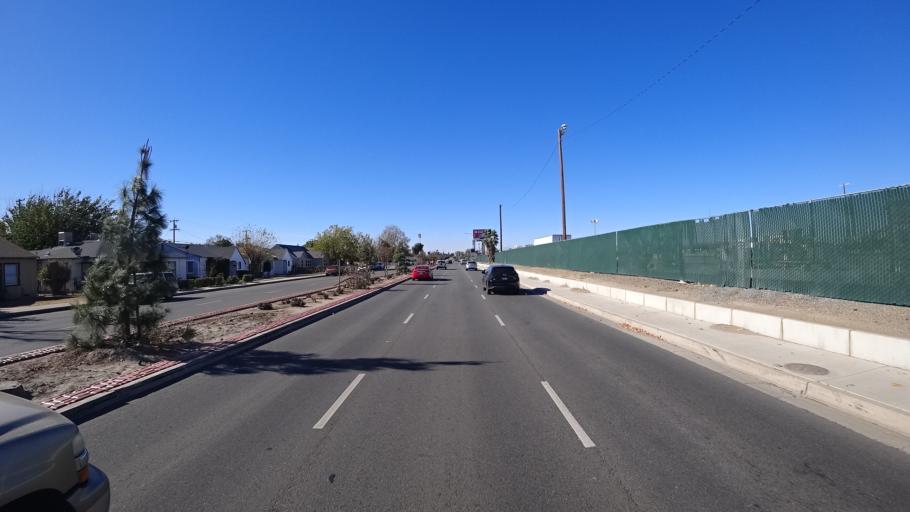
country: US
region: California
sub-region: Kern County
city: Bakersfield
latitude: 35.3686
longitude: -119.0350
